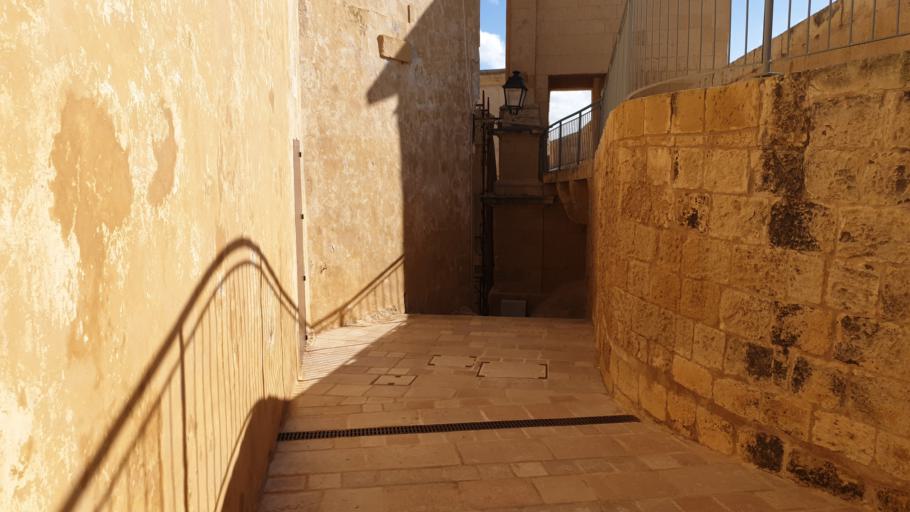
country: MT
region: Victoria
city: Victoria
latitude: 36.0463
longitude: 14.2390
